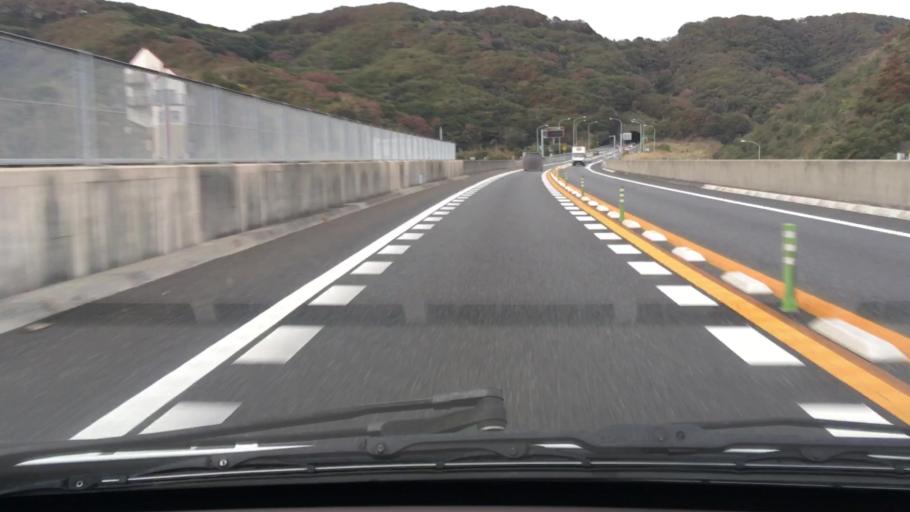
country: JP
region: Chiba
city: Futtsu
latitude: 35.1696
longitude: 139.8303
